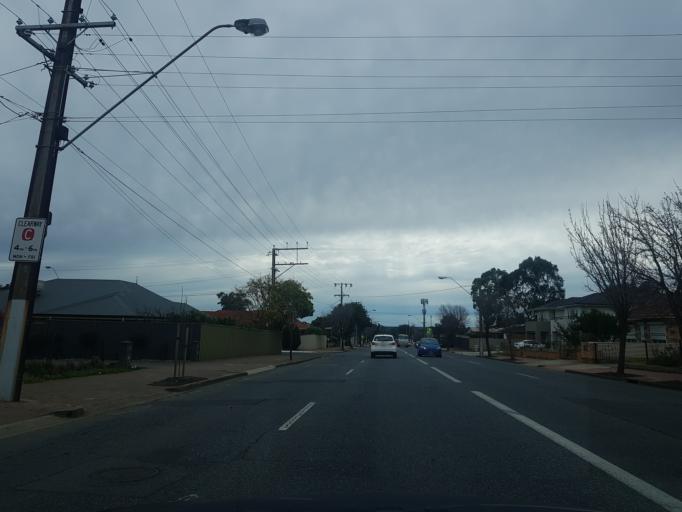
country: AU
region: South Australia
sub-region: Campbelltown
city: Hectorville
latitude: -34.8993
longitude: 138.6750
